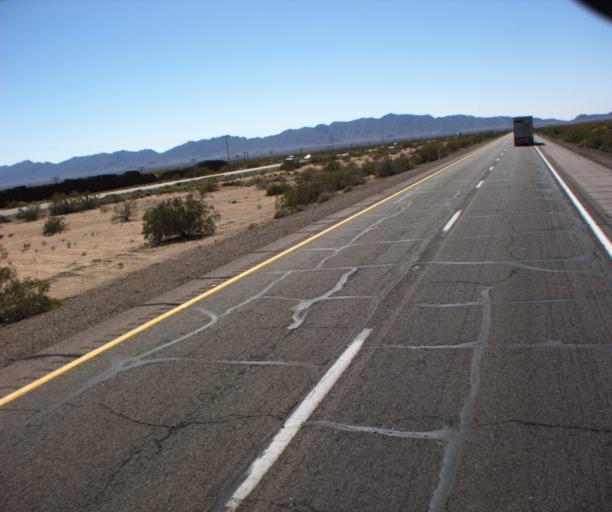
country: US
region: Arizona
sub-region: Yuma County
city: Wellton
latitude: 32.7682
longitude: -113.6165
